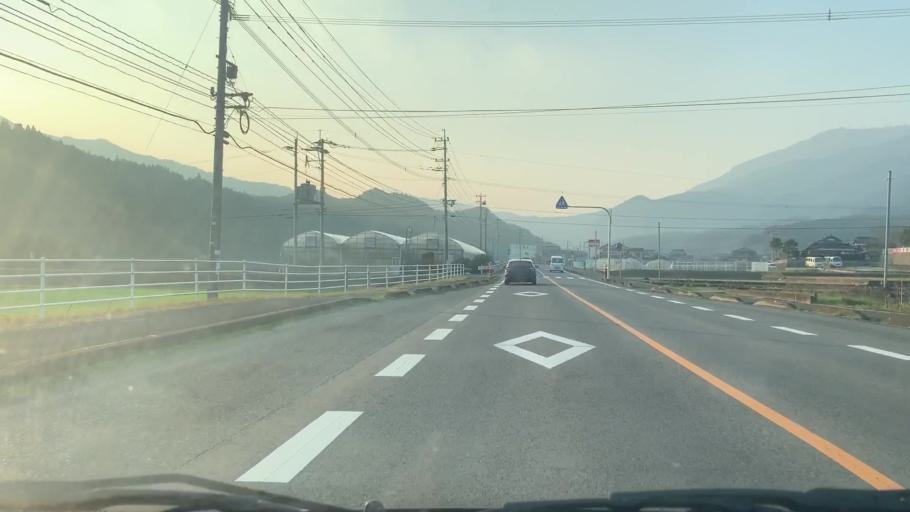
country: JP
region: Saga Prefecture
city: Takeocho-takeo
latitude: 33.2596
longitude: 130.0650
